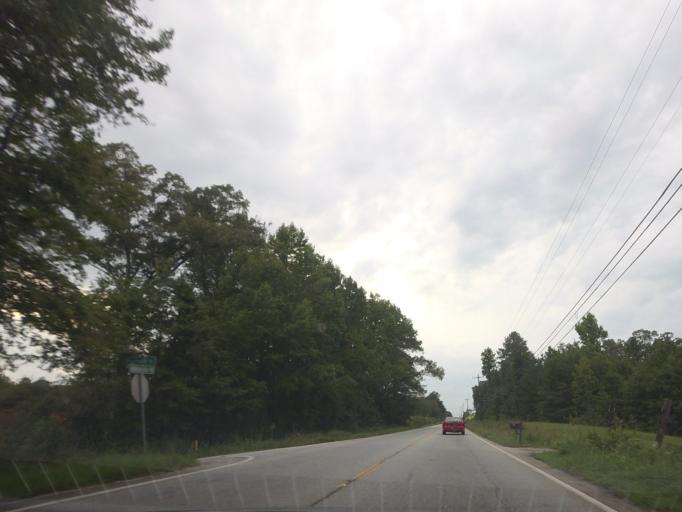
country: US
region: Georgia
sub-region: Bibb County
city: Macon
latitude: 32.8215
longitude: -83.5274
